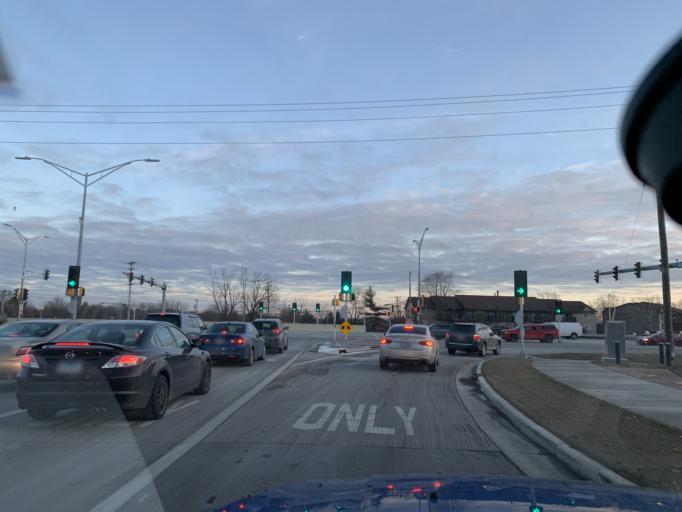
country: US
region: Wisconsin
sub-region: Dane County
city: Shorewood Hills
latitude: 43.0312
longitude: -89.4615
